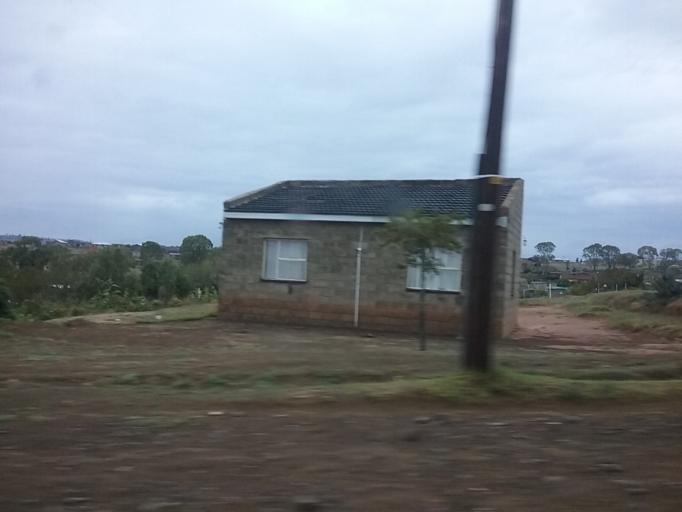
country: LS
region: Berea
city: Teyateyaneng
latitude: -29.1275
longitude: 27.7541
